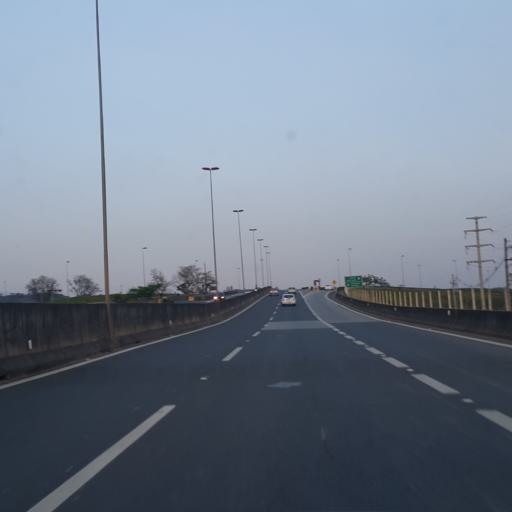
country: BR
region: Sao Paulo
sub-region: Vinhedo
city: Vinhedo
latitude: -23.0618
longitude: -46.9971
